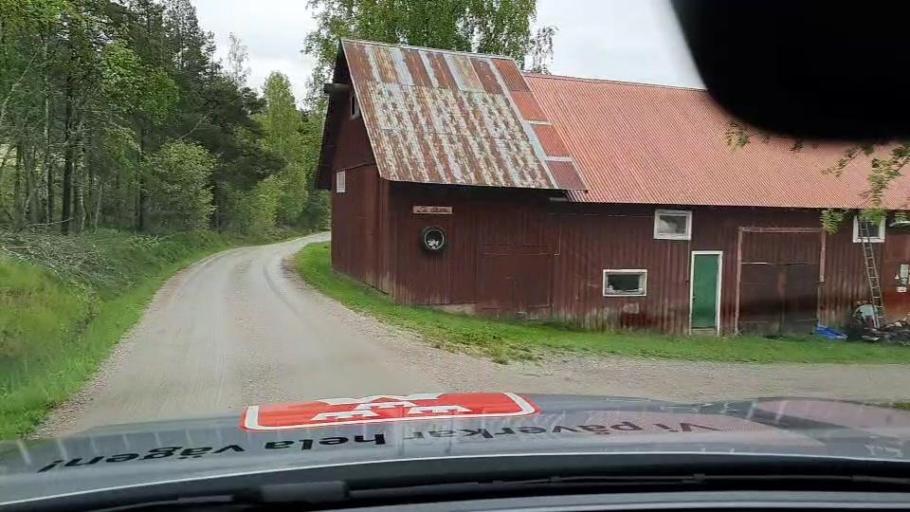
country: SE
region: Soedermanland
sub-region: Nykopings Kommun
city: Svalsta
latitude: 58.6272
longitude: 16.9399
